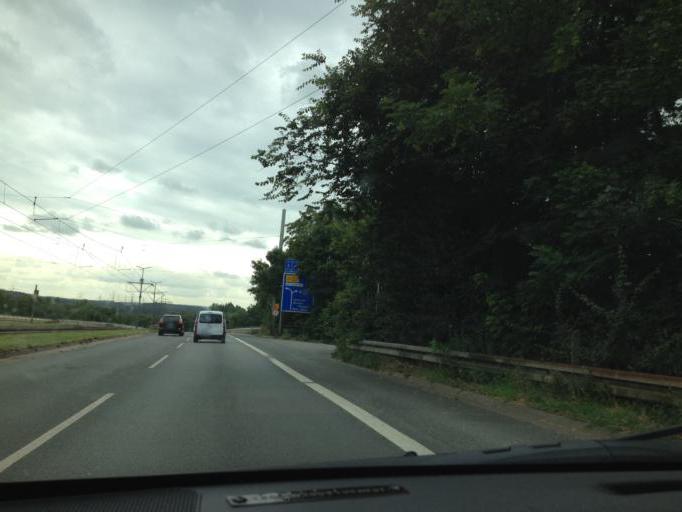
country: DE
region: North Rhine-Westphalia
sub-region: Regierungsbezirk Arnsberg
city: Bochum
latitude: 51.4673
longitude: 7.2713
